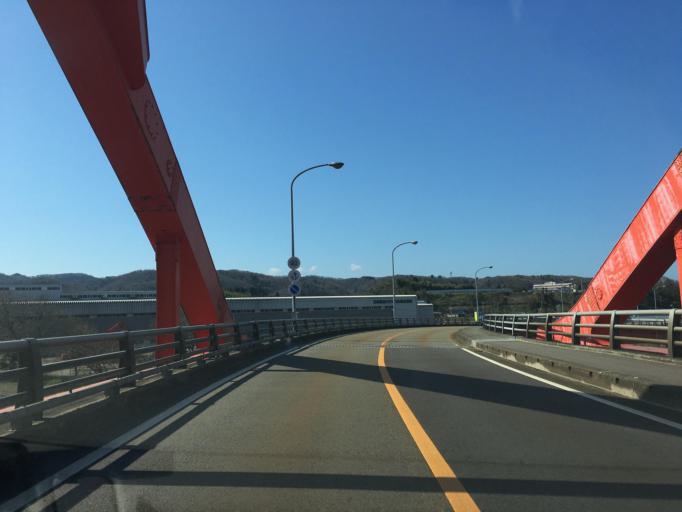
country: JP
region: Toyama
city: Nishishinminato
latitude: 36.7804
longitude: 137.0488
